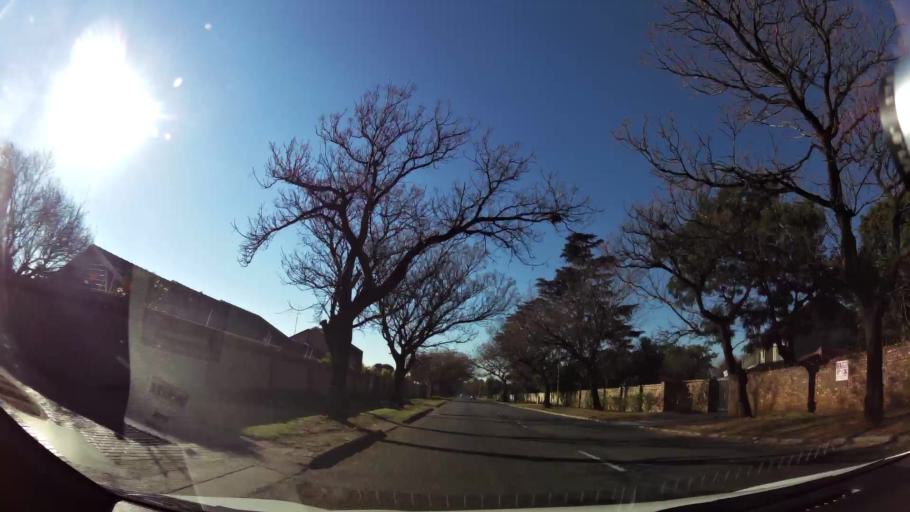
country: ZA
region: Gauteng
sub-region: Ekurhuleni Metropolitan Municipality
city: Germiston
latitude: -26.2838
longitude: 28.1164
